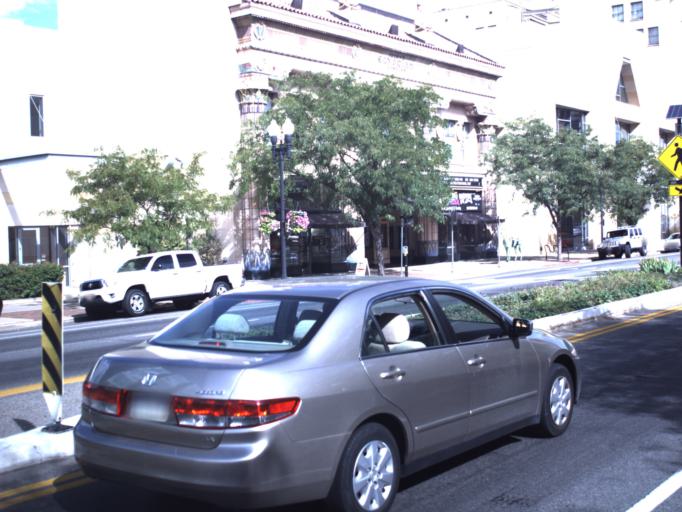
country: US
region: Utah
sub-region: Weber County
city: Ogden
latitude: 41.2214
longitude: -111.9704
